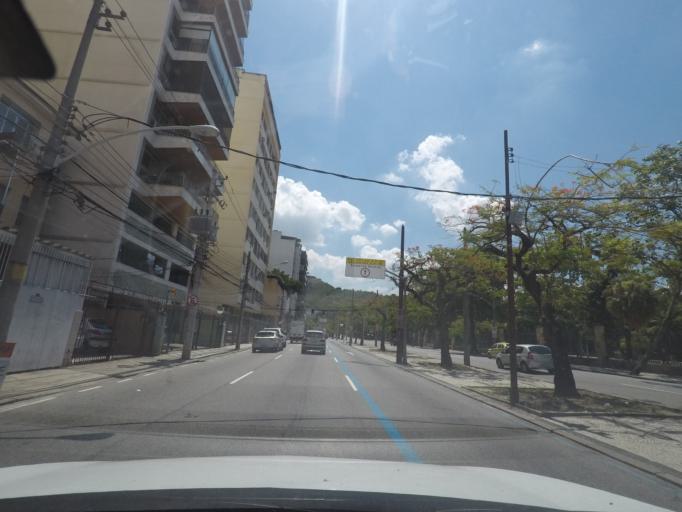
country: BR
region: Rio de Janeiro
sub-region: Rio De Janeiro
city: Rio de Janeiro
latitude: -22.9169
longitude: -43.2591
